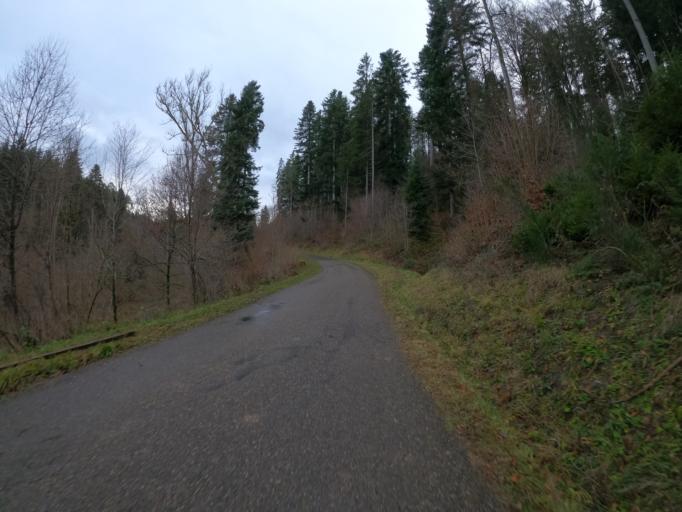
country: DE
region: Baden-Wuerttemberg
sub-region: Regierungsbezirk Stuttgart
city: Waschenbeuren
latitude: 48.7675
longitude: 9.7121
